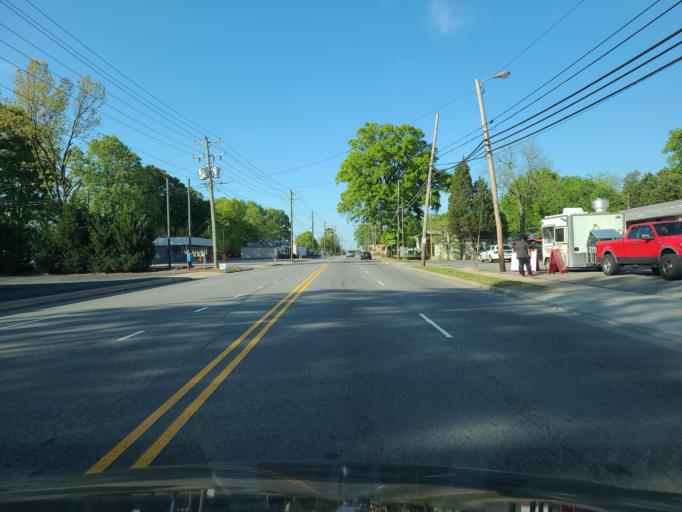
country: US
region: North Carolina
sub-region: Mecklenburg County
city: Charlotte
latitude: 35.2557
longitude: -80.8237
